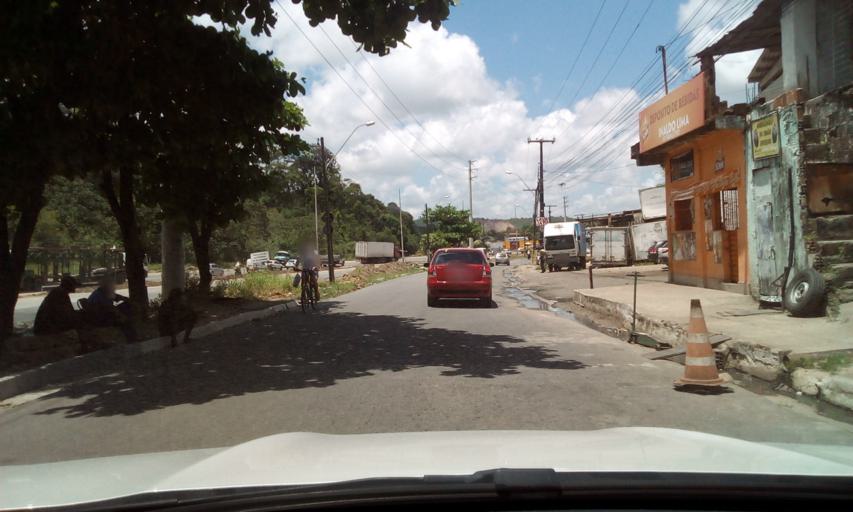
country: BR
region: Pernambuco
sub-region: Sao Lourenco Da Mata
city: Sao Lourenco da Mata
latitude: -7.9975
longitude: -34.9392
